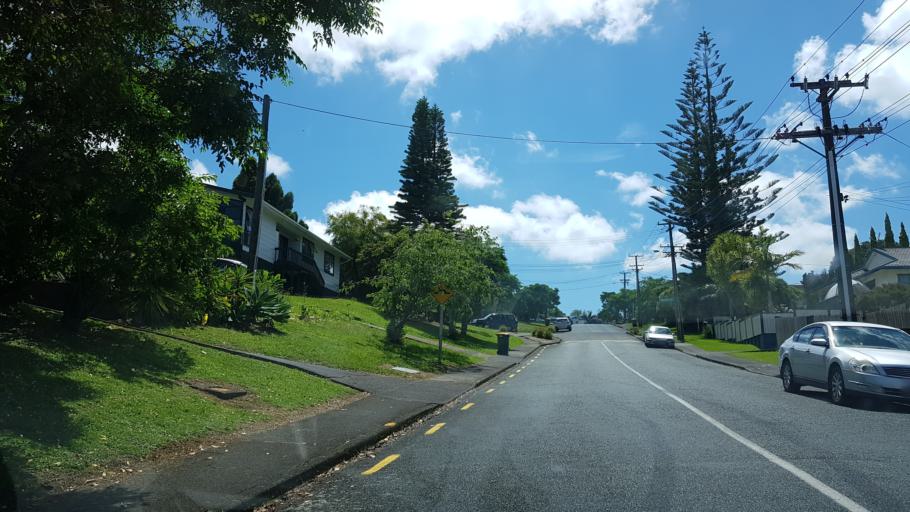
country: NZ
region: Auckland
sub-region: Auckland
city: North Shore
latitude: -36.7839
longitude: 174.7162
